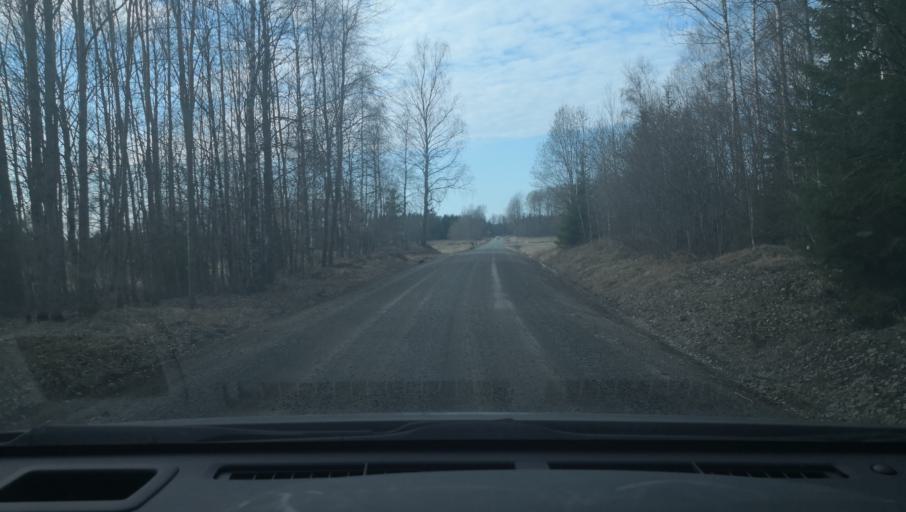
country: SE
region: Uppsala
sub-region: Heby Kommun
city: Heby
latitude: 59.8572
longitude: 16.8560
